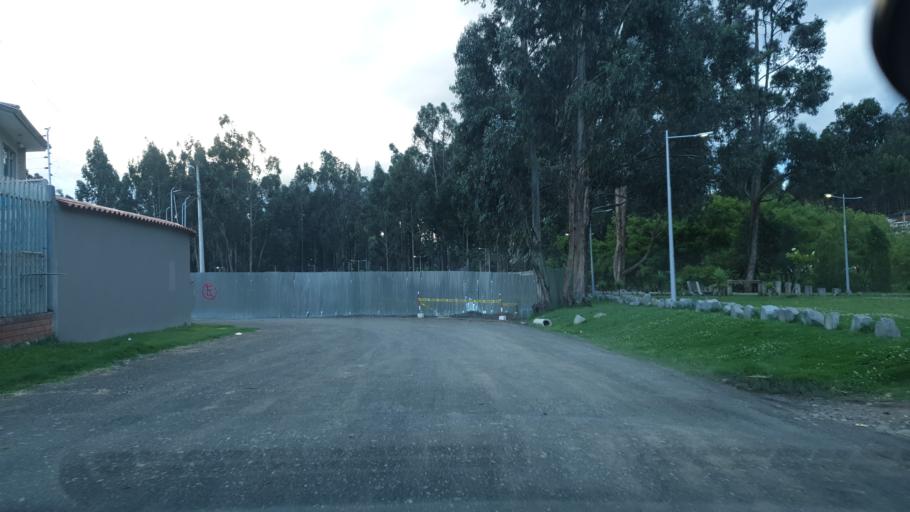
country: EC
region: Azuay
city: Cuenca
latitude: -2.9198
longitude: -79.0286
